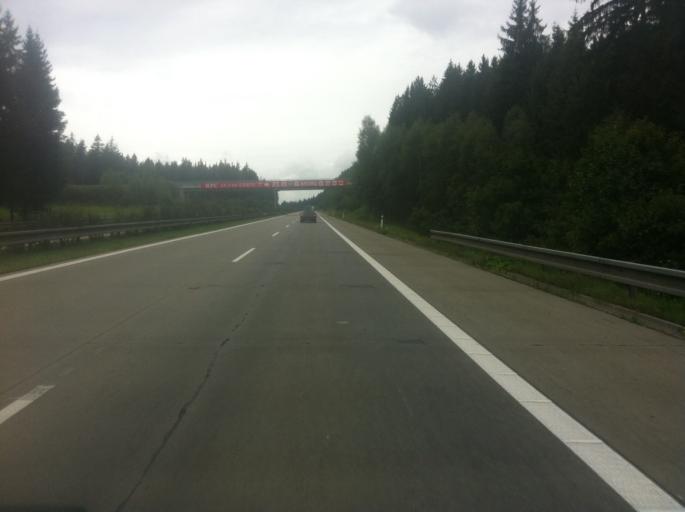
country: DE
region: Bavaria
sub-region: Upper Palatinate
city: Waidhaus
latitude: 49.6606
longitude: 12.5611
